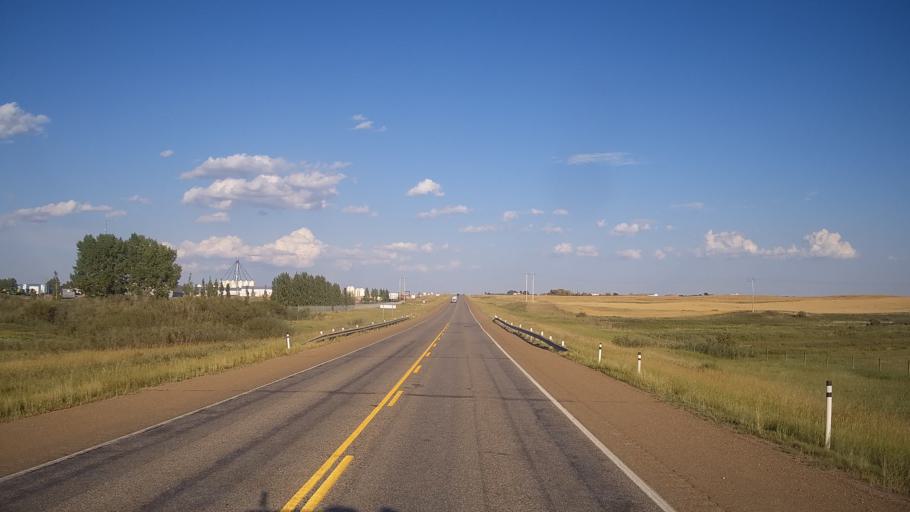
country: CA
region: Alberta
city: Hanna
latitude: 51.6334
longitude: -111.9364
